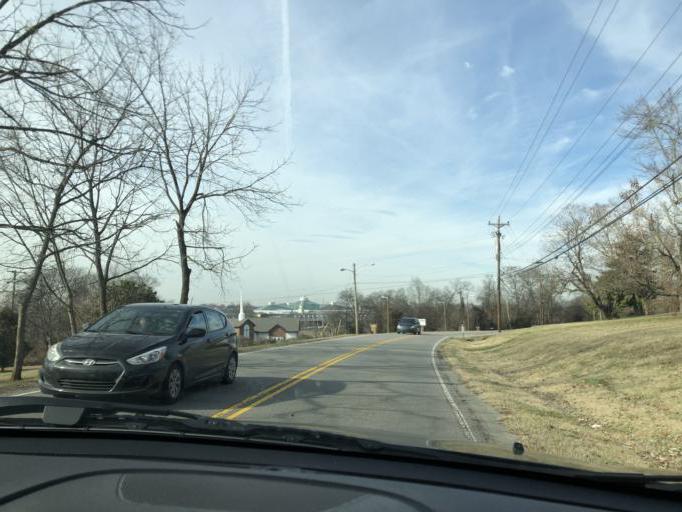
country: US
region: Tennessee
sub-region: Davidson County
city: Lakewood
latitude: 36.2092
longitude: -86.6850
